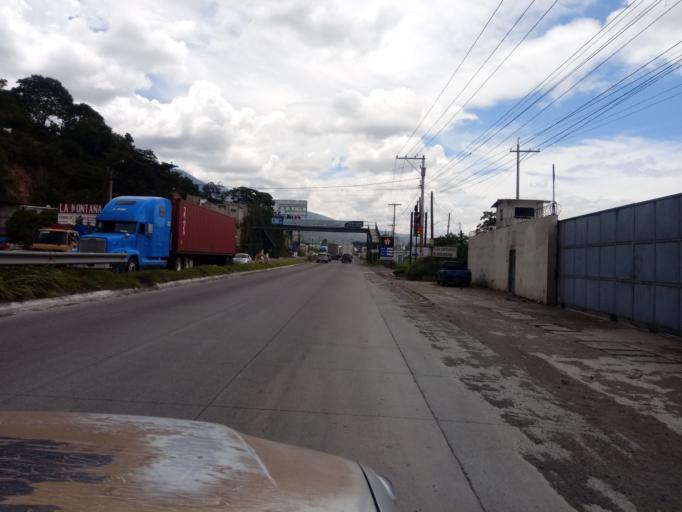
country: GT
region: Escuintla
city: San Vicente Pacaya
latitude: 14.4571
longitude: -90.6433
